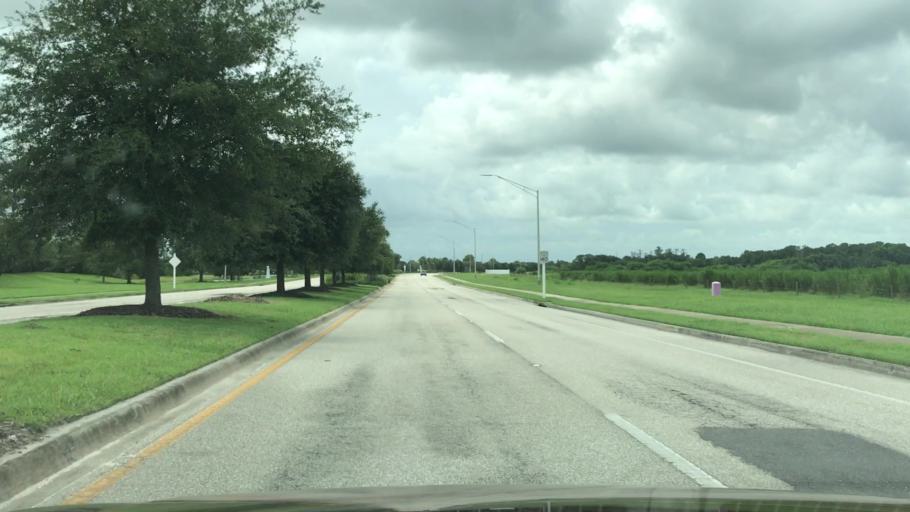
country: US
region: Florida
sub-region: Sarasota County
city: The Meadows
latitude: 27.4420
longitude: -82.4141
